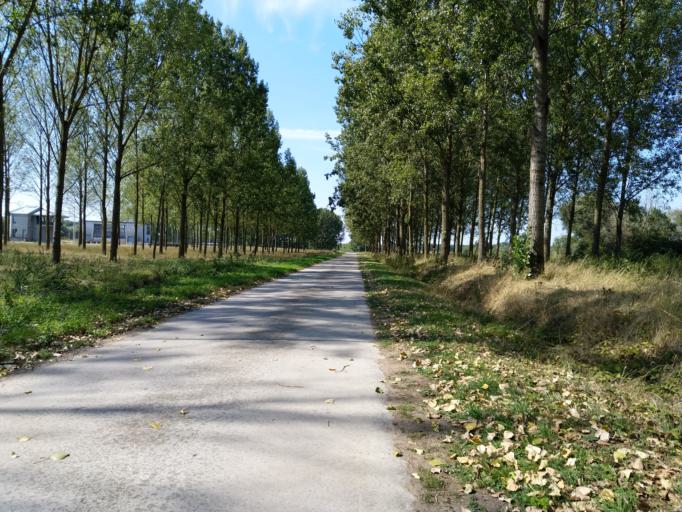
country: BE
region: Wallonia
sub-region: Province du Hainaut
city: Mons
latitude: 50.4791
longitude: 3.9843
